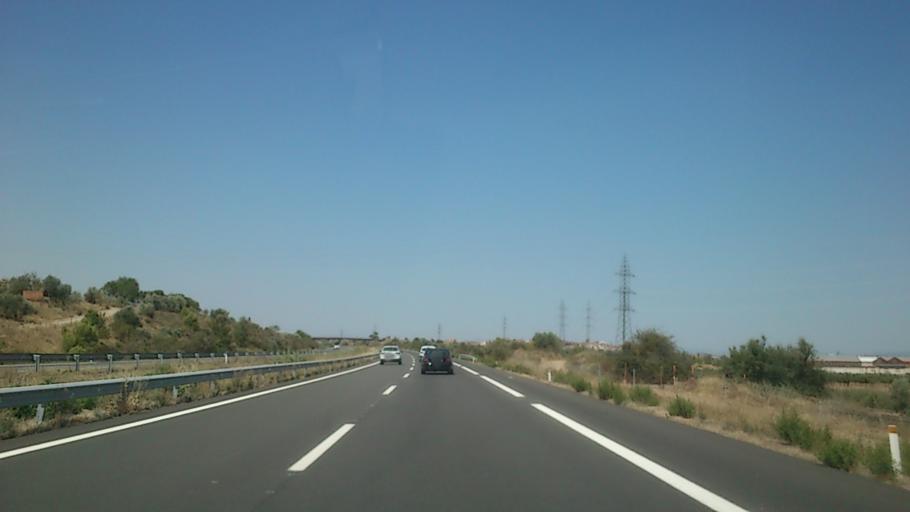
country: ES
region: La Rioja
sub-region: Provincia de La Rioja
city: Calahorra
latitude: 42.2798
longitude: -1.9389
